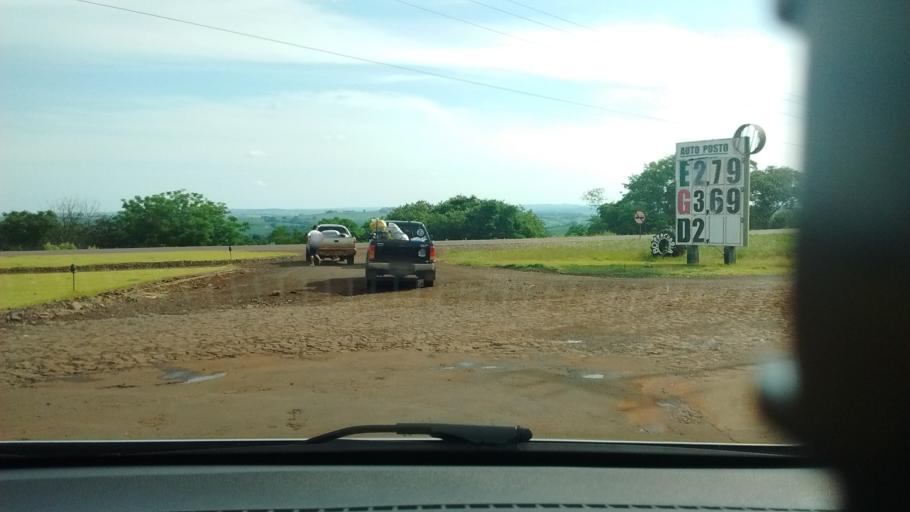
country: BR
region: Parana
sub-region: Corbelia
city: Corbelia
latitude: -24.5567
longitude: -52.9896
